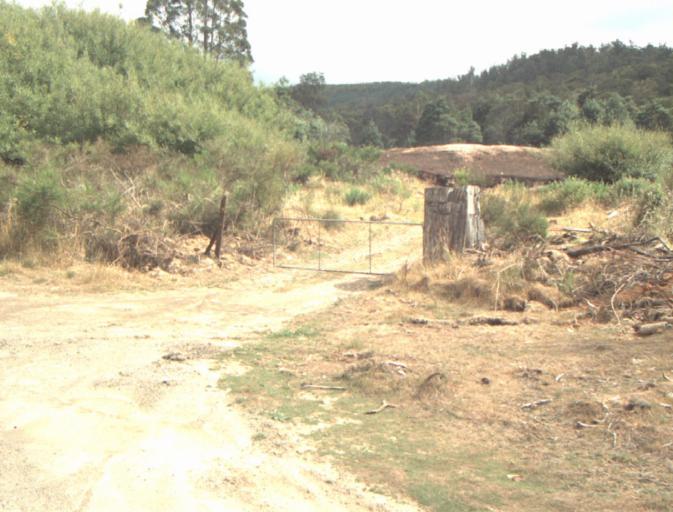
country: AU
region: Tasmania
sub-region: Northern Midlands
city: Evandale
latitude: -41.4498
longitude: 147.4792
